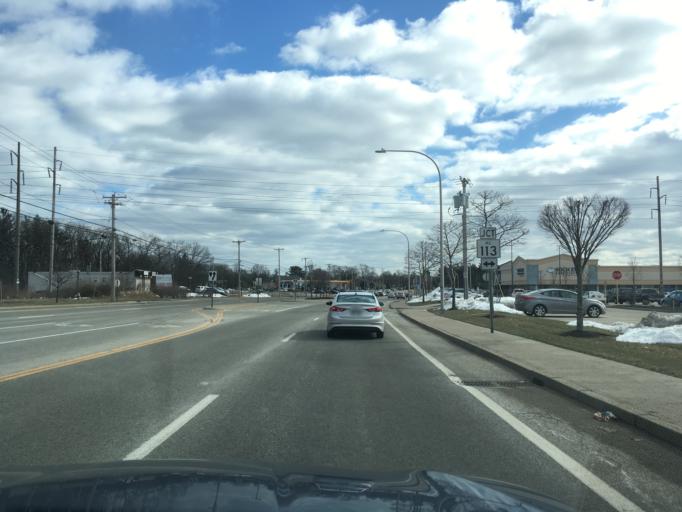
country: US
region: Rhode Island
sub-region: Kent County
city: Warwick
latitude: 41.7194
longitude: -71.4645
